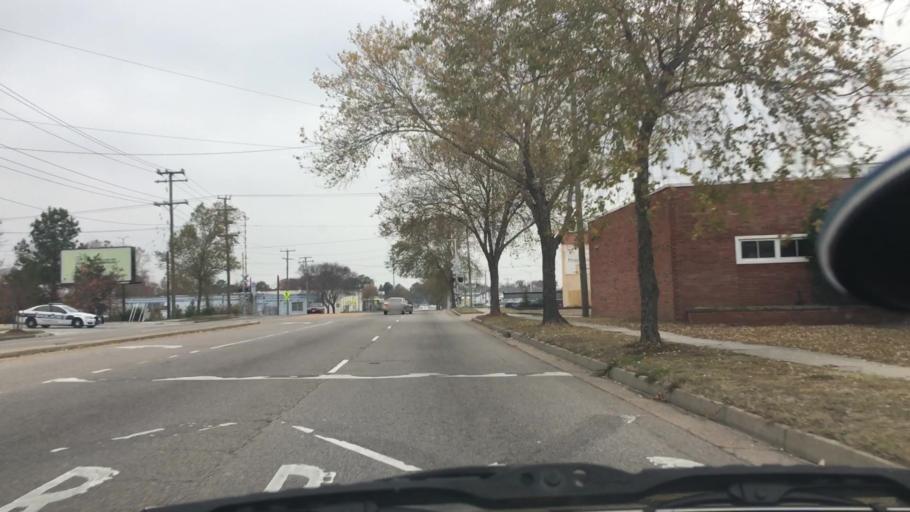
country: US
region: Virginia
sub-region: City of Norfolk
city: Norfolk
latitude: 36.8640
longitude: -76.2449
